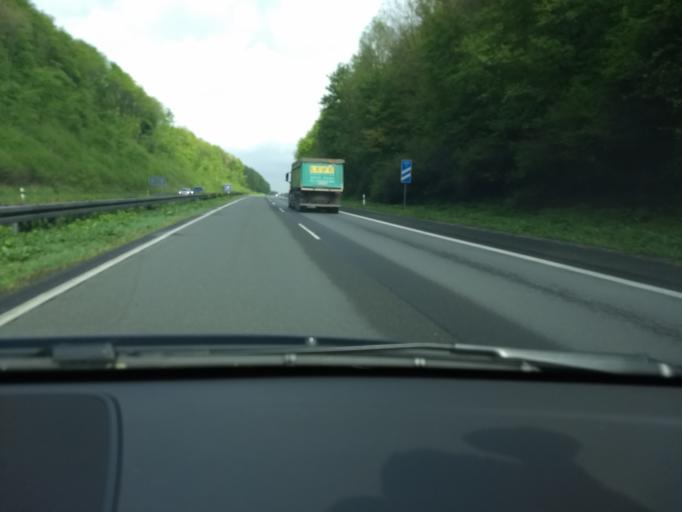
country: DE
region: North Rhine-Westphalia
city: Wickede
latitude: 51.5134
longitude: 7.9049
